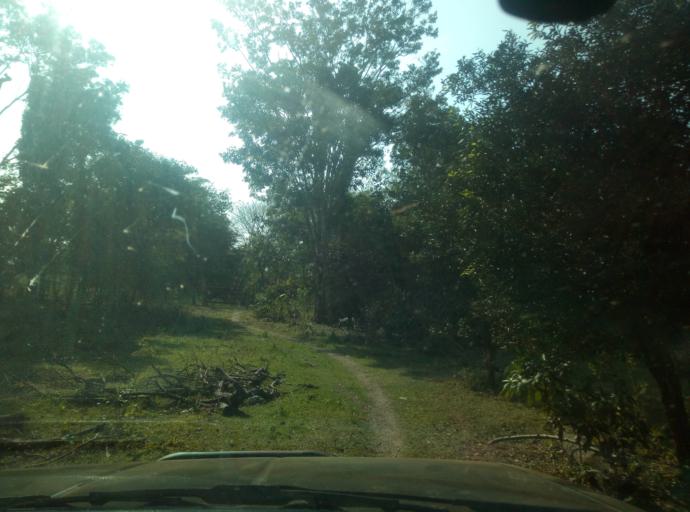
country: PY
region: Caaguazu
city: San Joaquin
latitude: -25.1576
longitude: -56.1320
